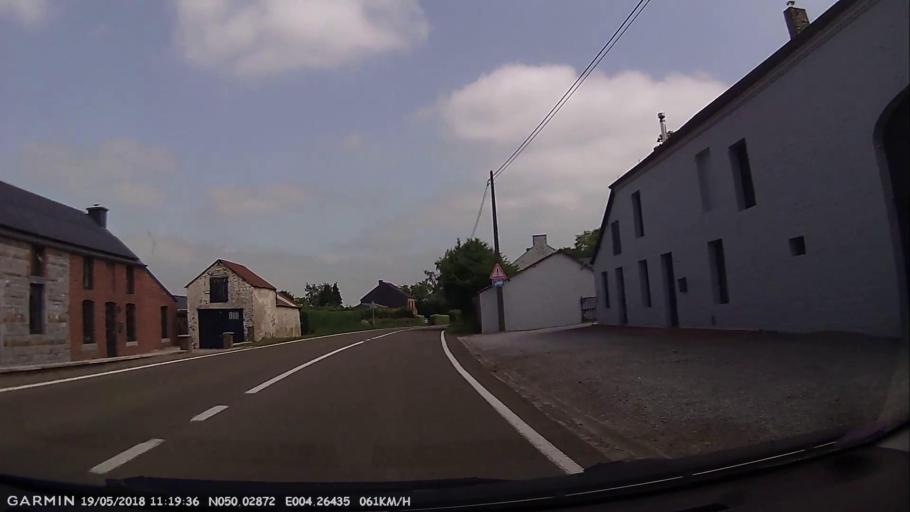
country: BE
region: Wallonia
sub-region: Province du Hainaut
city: Chimay
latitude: 50.0289
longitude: 4.2645
